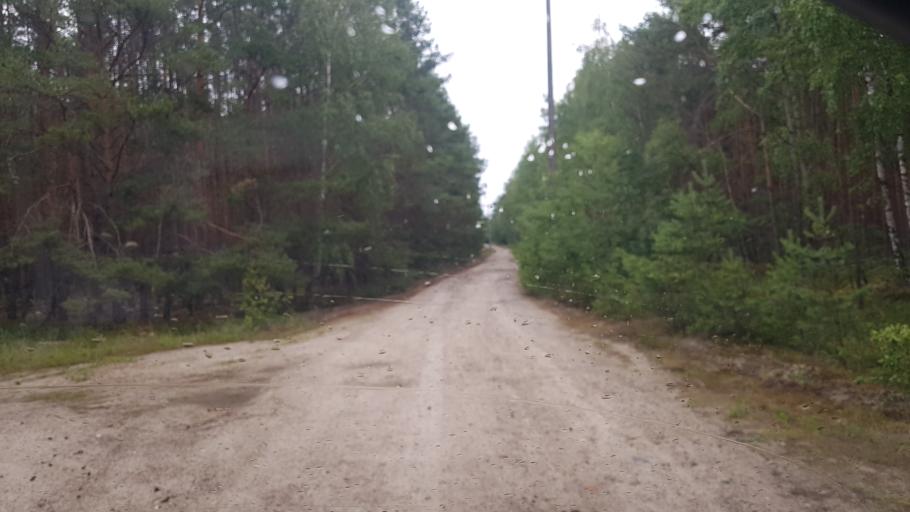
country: DE
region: Brandenburg
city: Finsterwalde
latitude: 51.5890
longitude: 13.7255
